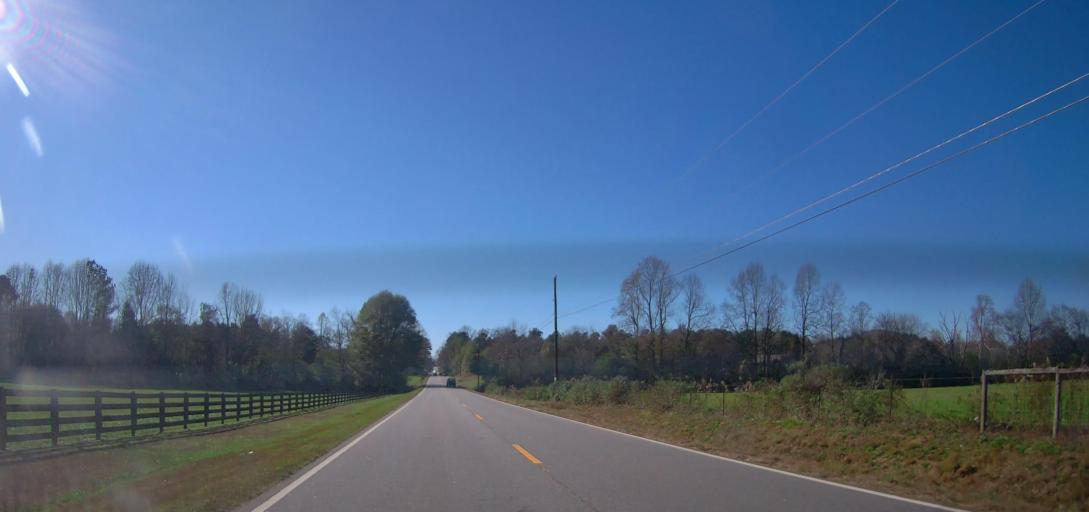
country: US
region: Georgia
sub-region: White County
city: Cleveland
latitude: 34.4774
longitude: -83.7604
